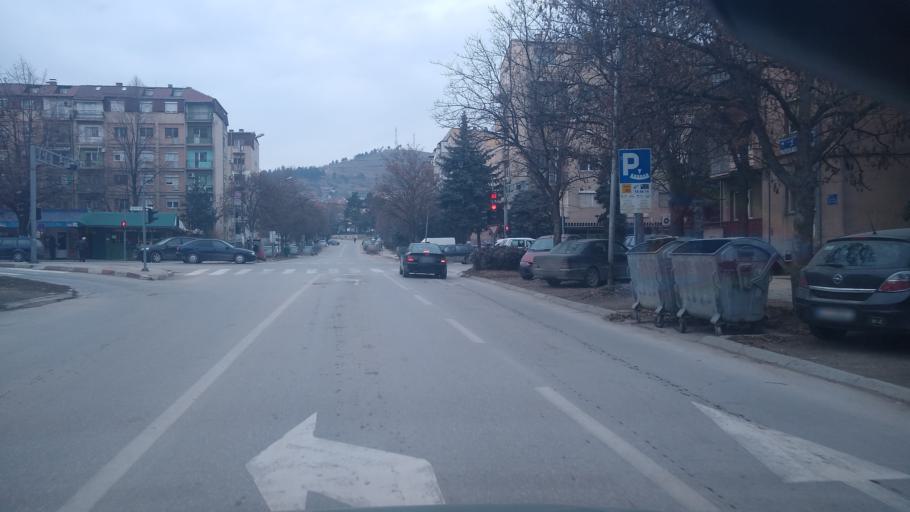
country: MK
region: Bitola
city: Bitola
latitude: 41.0348
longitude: 21.3403
